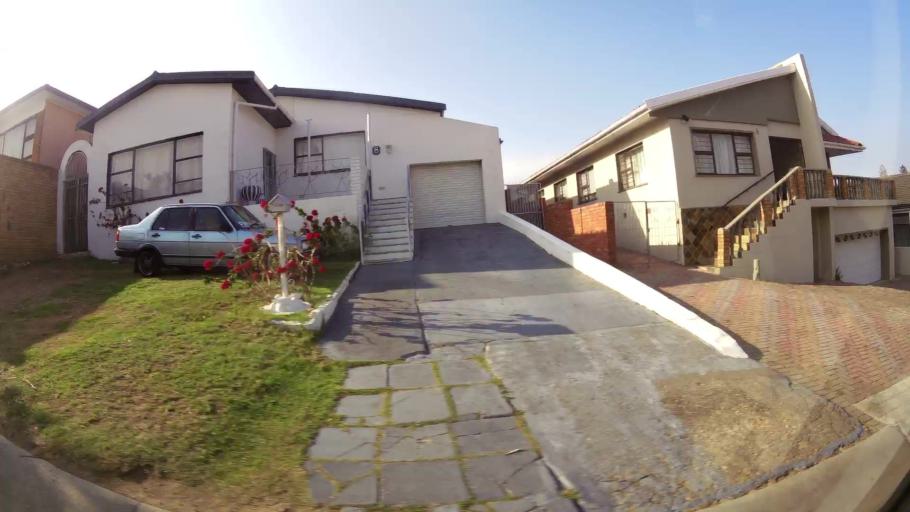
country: ZA
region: Eastern Cape
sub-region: Nelson Mandela Bay Metropolitan Municipality
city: Port Elizabeth
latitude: -33.9254
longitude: 25.5424
